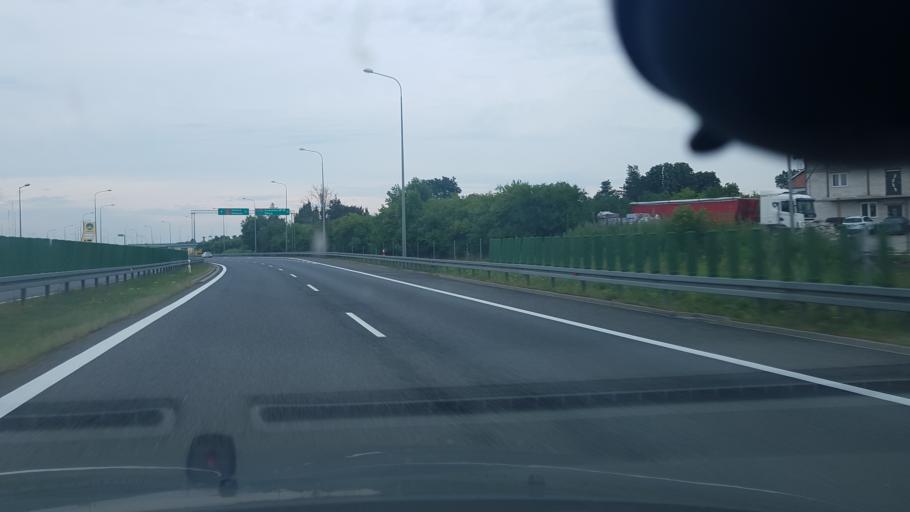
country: PL
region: Warmian-Masurian Voivodeship
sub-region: Powiat elblaski
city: Gronowo Gorne
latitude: 54.1348
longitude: 19.4549
